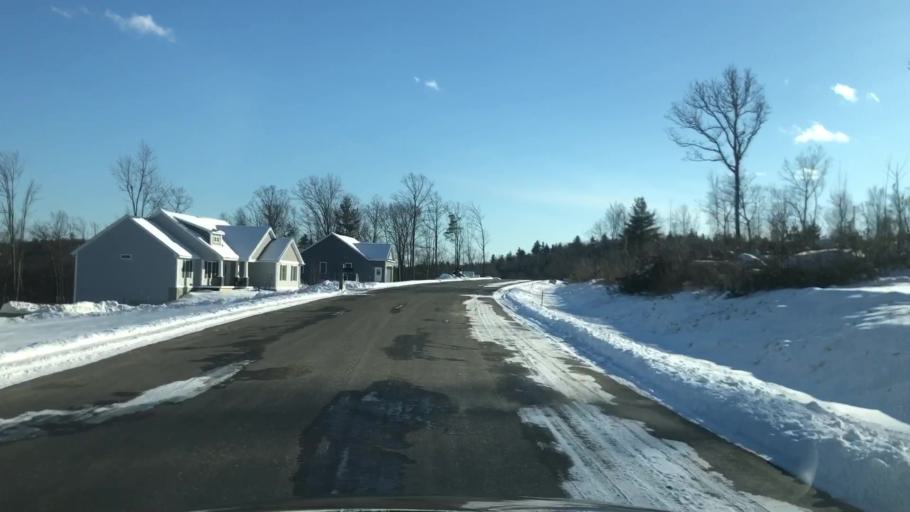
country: US
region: New Hampshire
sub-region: Hillsborough County
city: Wilton
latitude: 42.8052
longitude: -71.7105
